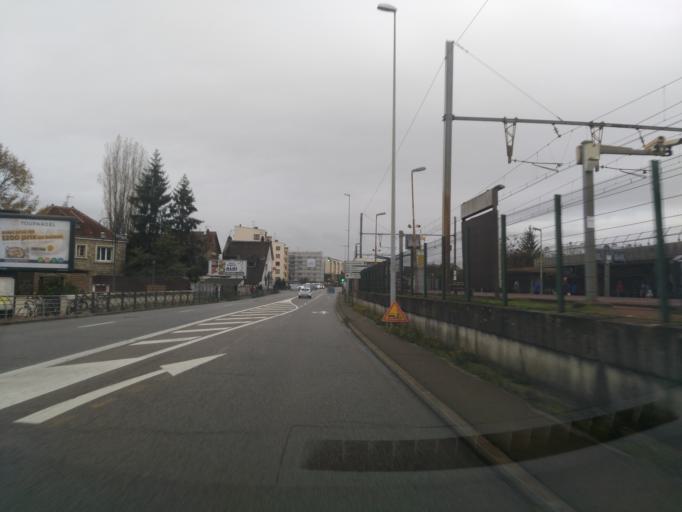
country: FR
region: Ile-de-France
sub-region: Departement des Yvelines
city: Les Clayes-sous-Bois
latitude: 48.8235
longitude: 1.9929
